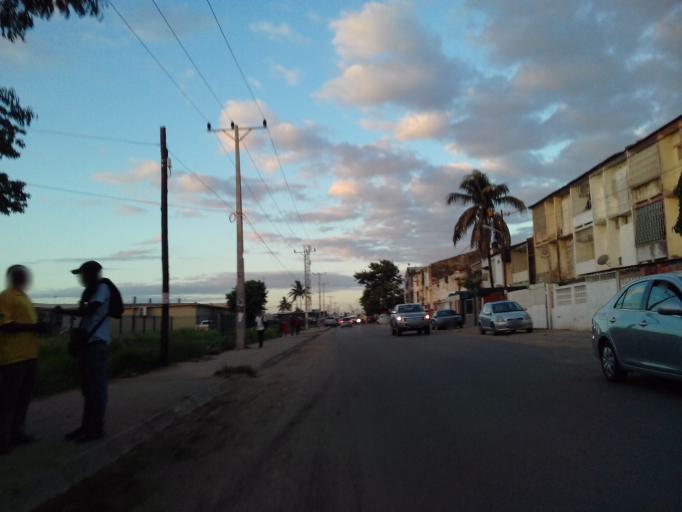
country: MZ
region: Maputo City
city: Maputo
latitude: -25.9528
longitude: 32.5803
